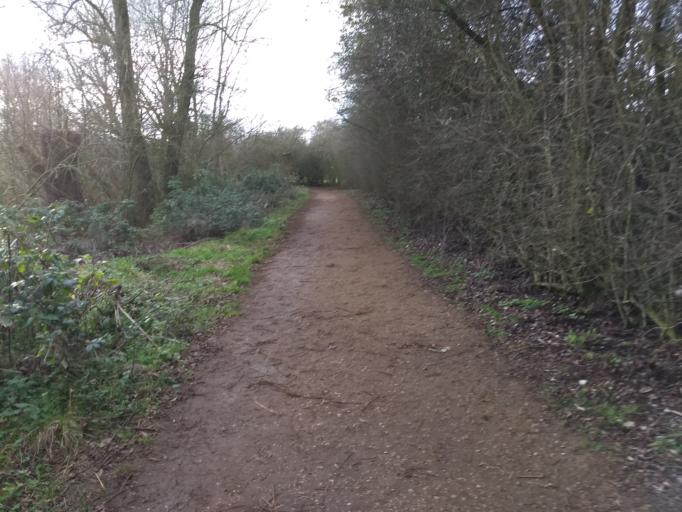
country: GB
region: England
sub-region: Bedford
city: Odell
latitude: 52.2054
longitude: -0.5981
